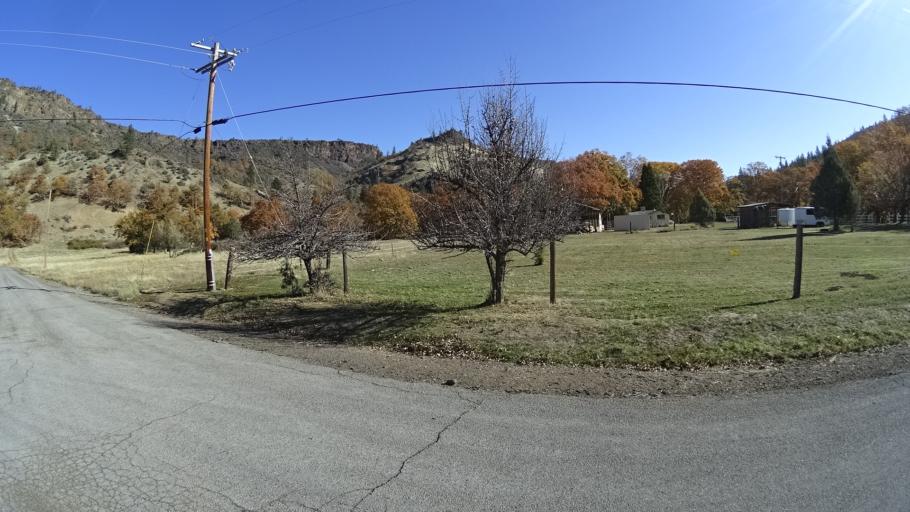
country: US
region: California
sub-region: Siskiyou County
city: Montague
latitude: 41.9661
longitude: -122.2607
